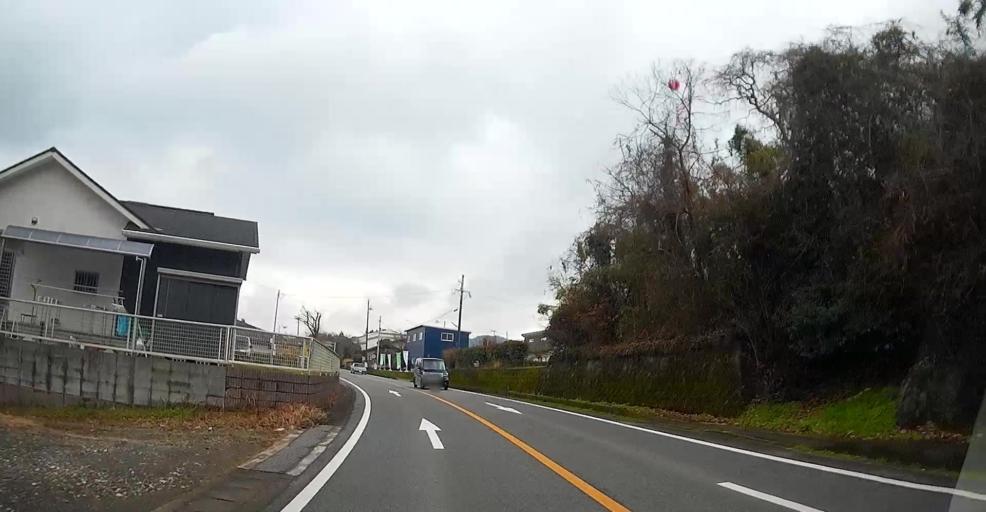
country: JP
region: Kumamoto
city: Matsubase
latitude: 32.6431
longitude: 130.7382
